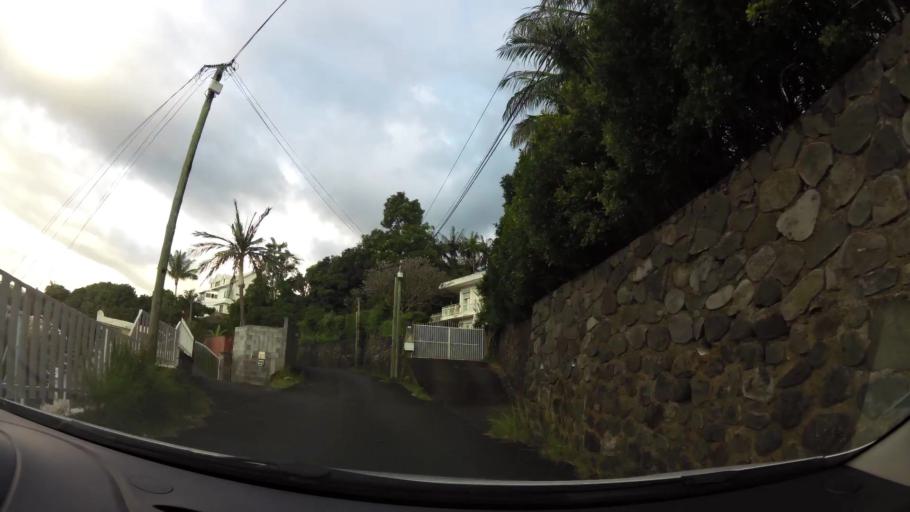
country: RE
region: Reunion
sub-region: Reunion
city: Saint-Denis
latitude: -20.9006
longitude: 55.4460
